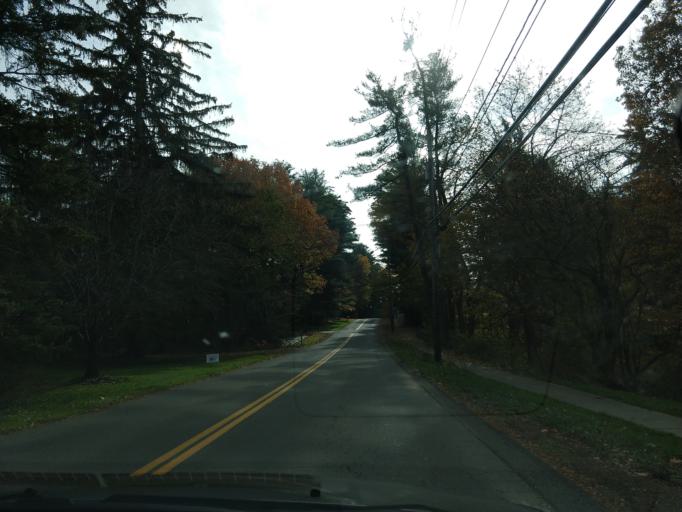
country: US
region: New York
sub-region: Tompkins County
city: Cayuga Heights
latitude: 42.4633
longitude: -76.4866
